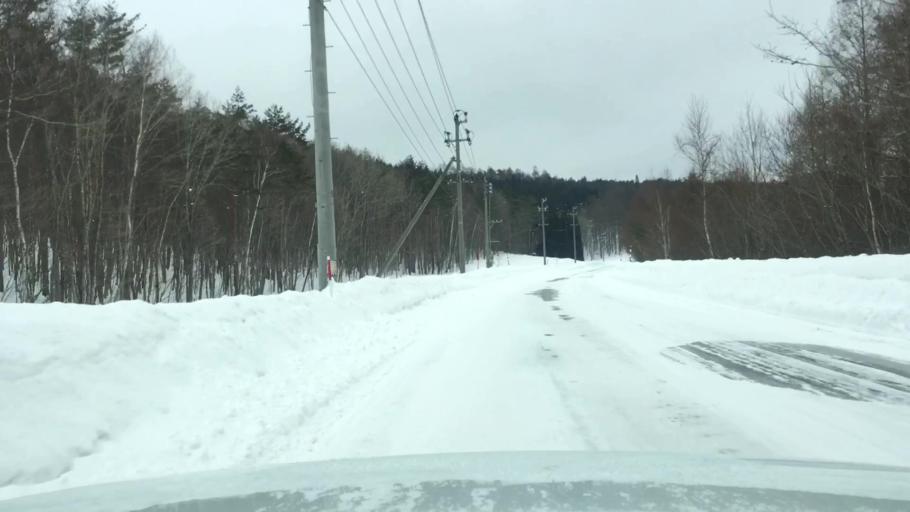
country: JP
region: Iwate
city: Shizukuishi
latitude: 39.9761
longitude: 141.0008
